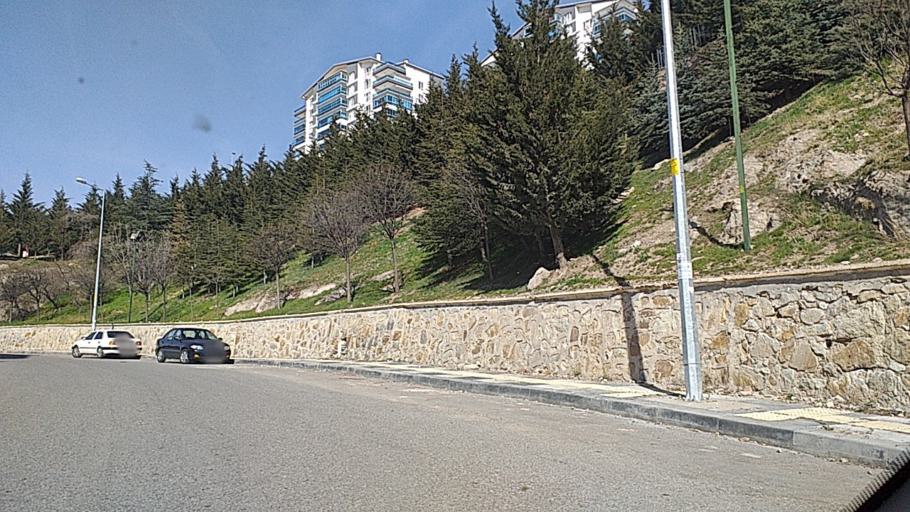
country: TR
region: Ankara
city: Ankara
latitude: 39.9895
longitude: 32.8157
